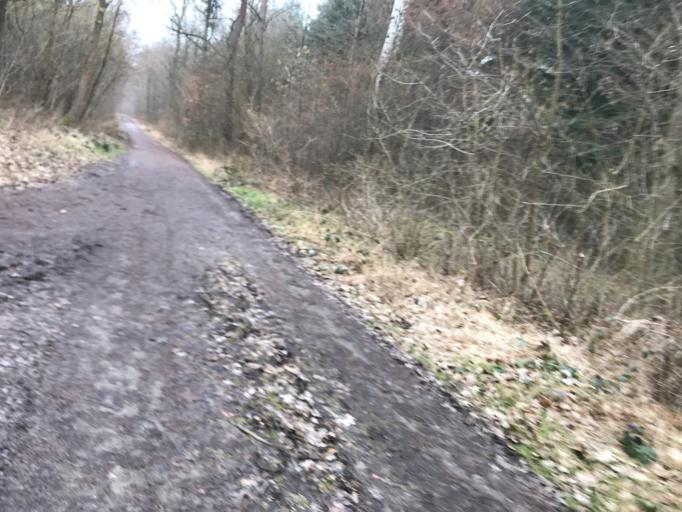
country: DE
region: Rheinland-Pfalz
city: Ober-Olm
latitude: 49.9630
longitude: 8.1804
